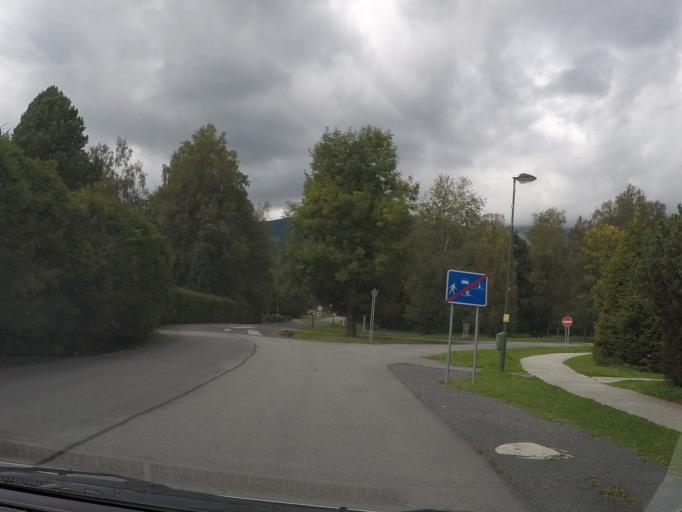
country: SK
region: Presovsky
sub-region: Okres Poprad
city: Nova Lesna
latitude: 49.1634
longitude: 20.2818
